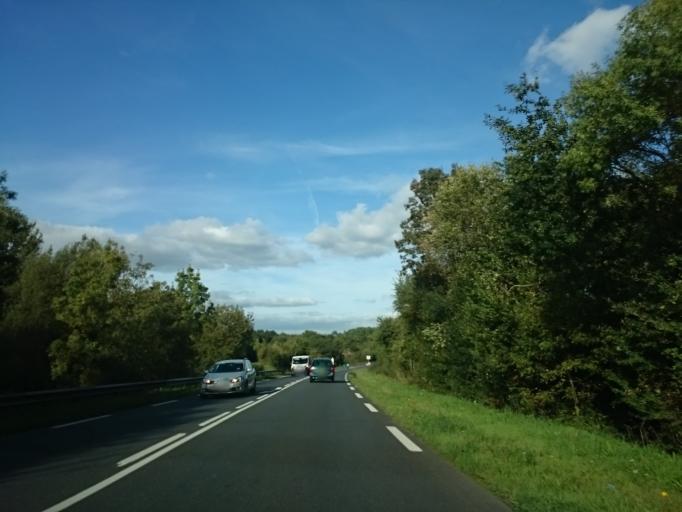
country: FR
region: Pays de la Loire
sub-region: Departement de la Loire-Atlantique
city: Indre
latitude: 47.2122
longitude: -1.6647
